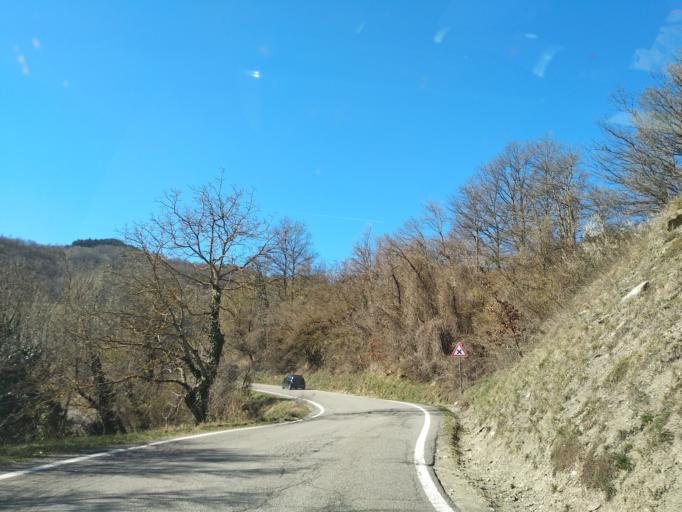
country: IT
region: Emilia-Romagna
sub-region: Provincia di Reggio Emilia
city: Ramiseto
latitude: 44.4120
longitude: 10.2706
